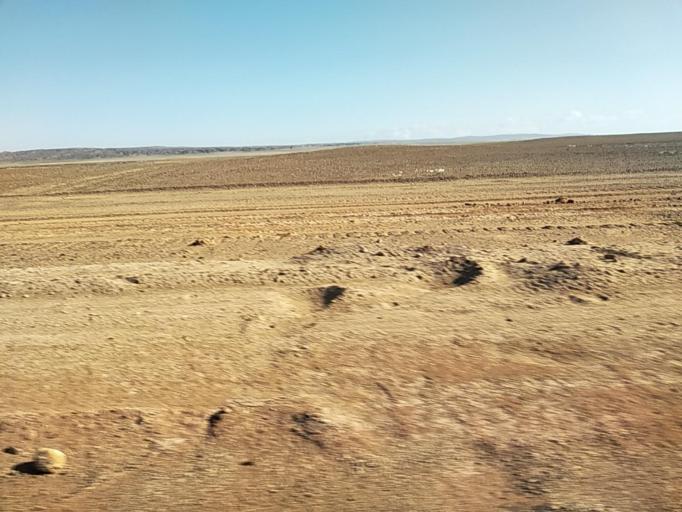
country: CL
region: Atacama
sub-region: Provincia de Copiapo
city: Copiapo
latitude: -27.3233
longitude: -70.8106
